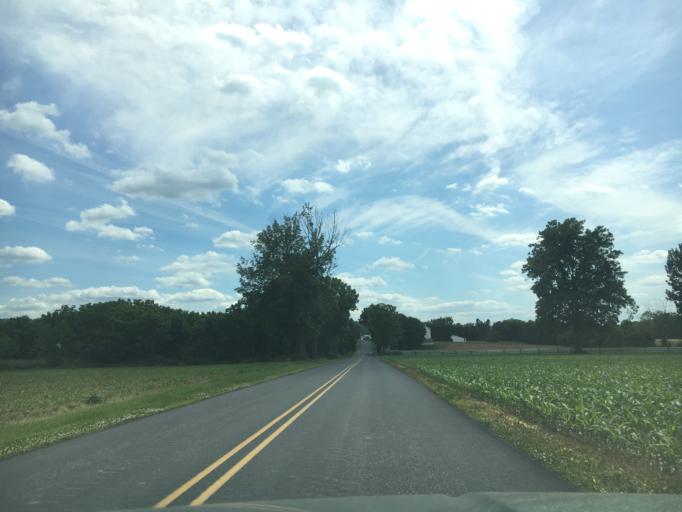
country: US
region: Pennsylvania
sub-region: Berks County
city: Fleetwood
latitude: 40.4626
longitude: -75.8144
